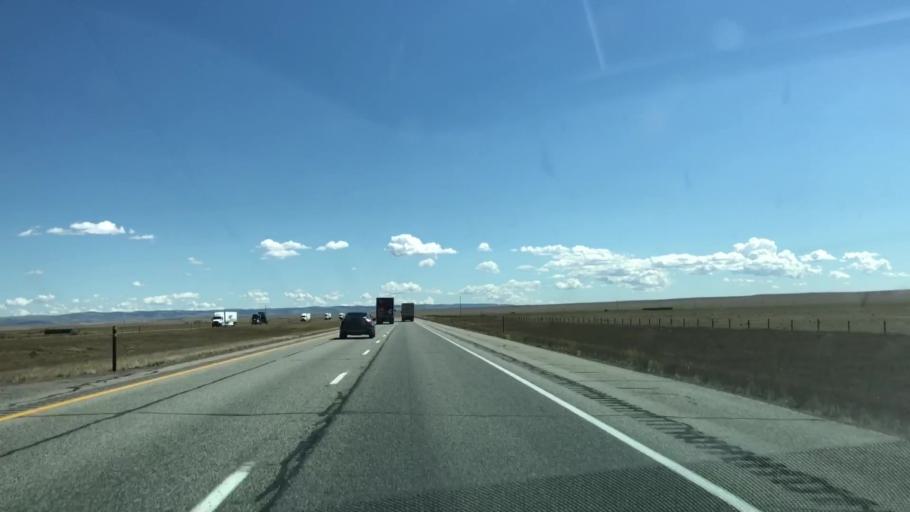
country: US
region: Wyoming
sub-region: Albany County
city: Laramie
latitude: 41.3775
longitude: -105.8048
